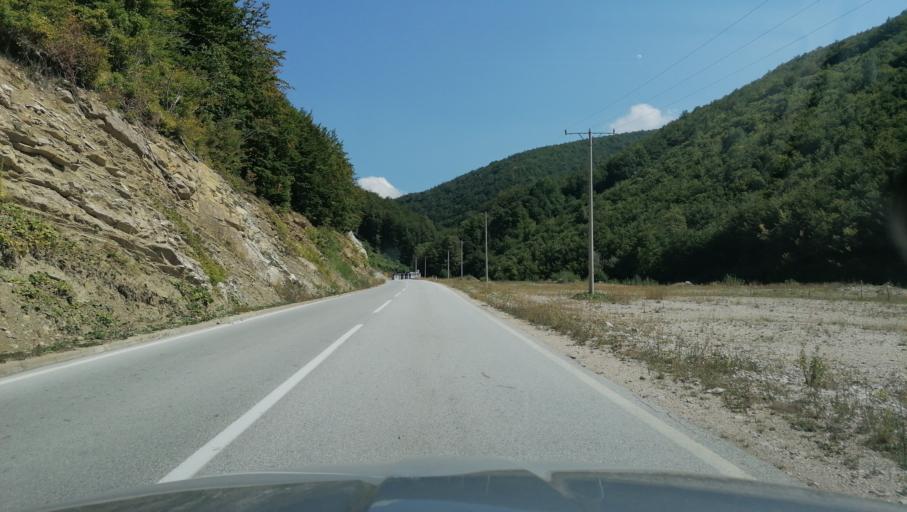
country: BA
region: Republika Srpska
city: Gacko
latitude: 43.2325
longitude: 18.5903
